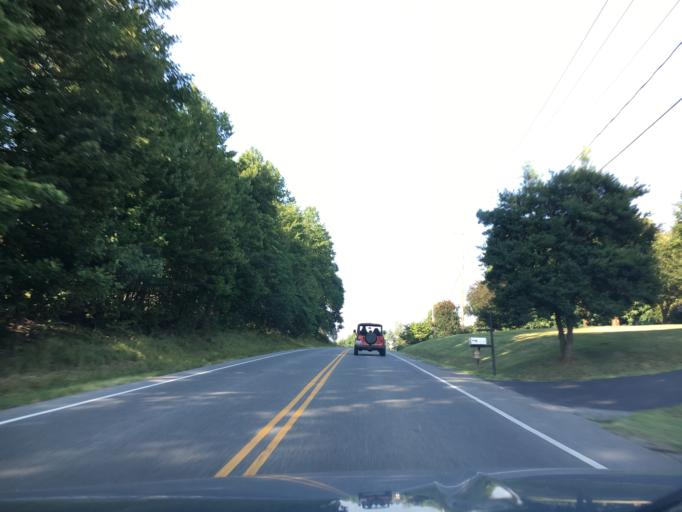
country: US
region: Virginia
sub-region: Franklin County
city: Henry Fork
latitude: 37.0086
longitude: -79.7893
